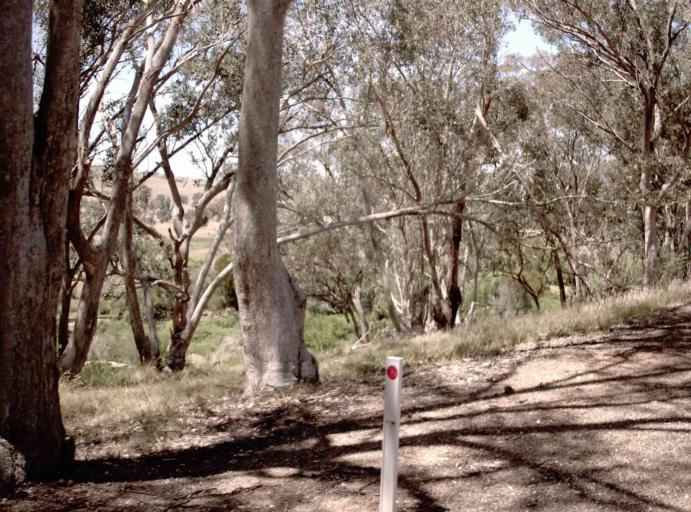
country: AU
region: Victoria
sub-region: East Gippsland
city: Bairnsdale
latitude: -37.2168
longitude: 147.7163
